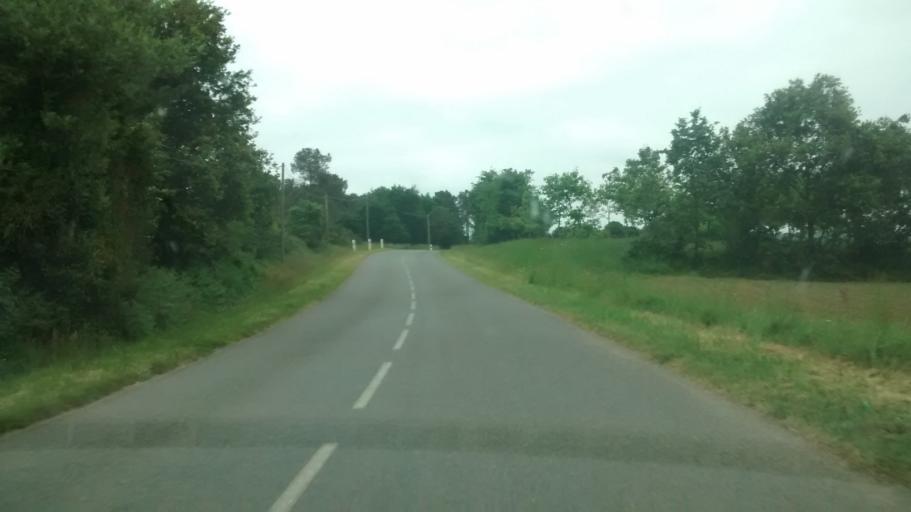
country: FR
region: Brittany
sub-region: Departement du Morbihan
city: Campeneac
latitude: 47.9663
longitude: -2.2837
